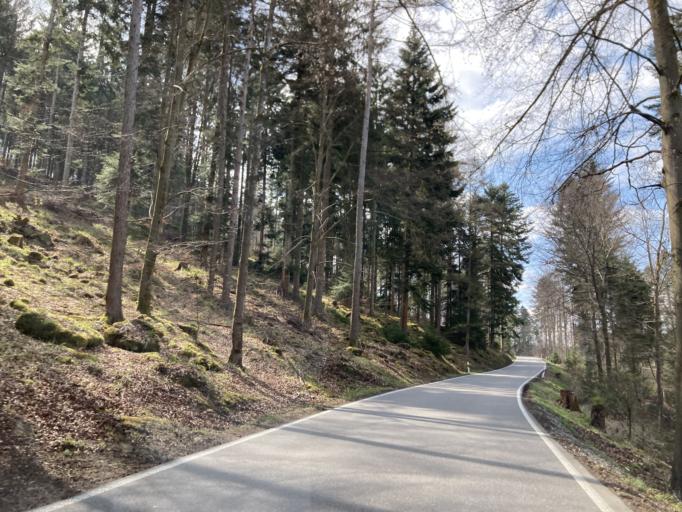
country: DE
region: Baden-Wuerttemberg
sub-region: Karlsruhe Region
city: Neuenburg
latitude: 48.8322
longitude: 8.5694
